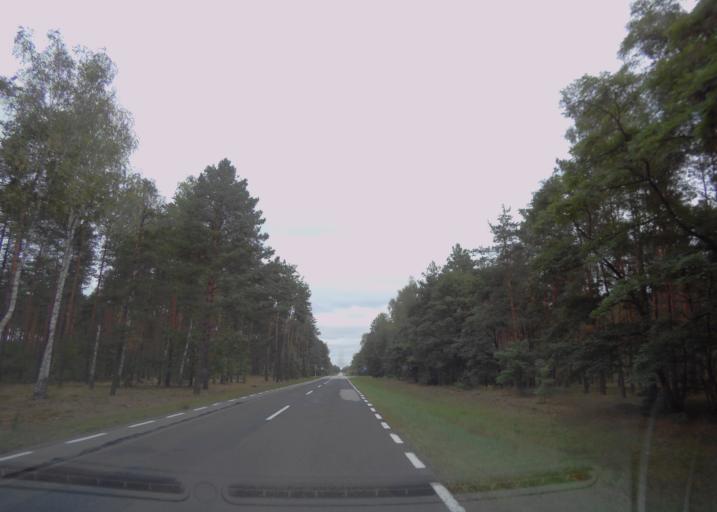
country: PL
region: Lublin Voivodeship
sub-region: Powiat wlodawski
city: Wlodawa
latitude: 51.4746
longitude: 23.5137
